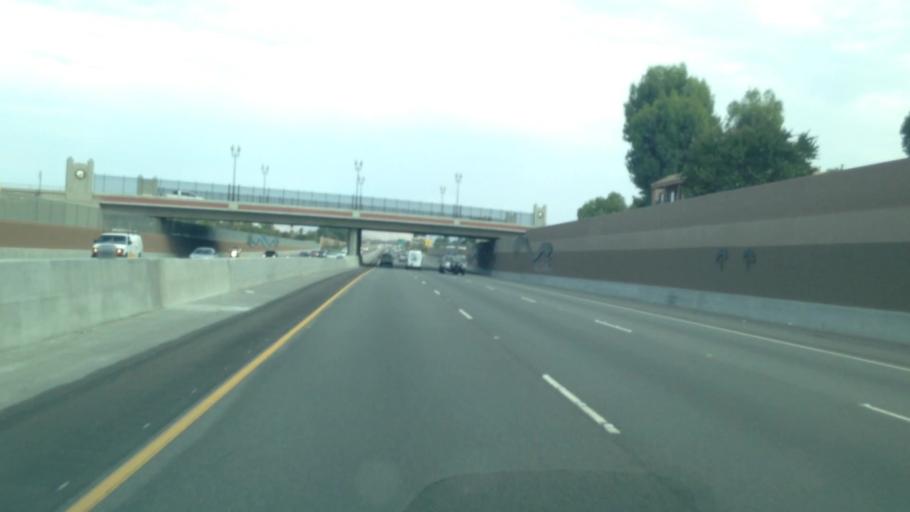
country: US
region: California
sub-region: Riverside County
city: Perris
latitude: 33.7912
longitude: -117.2273
